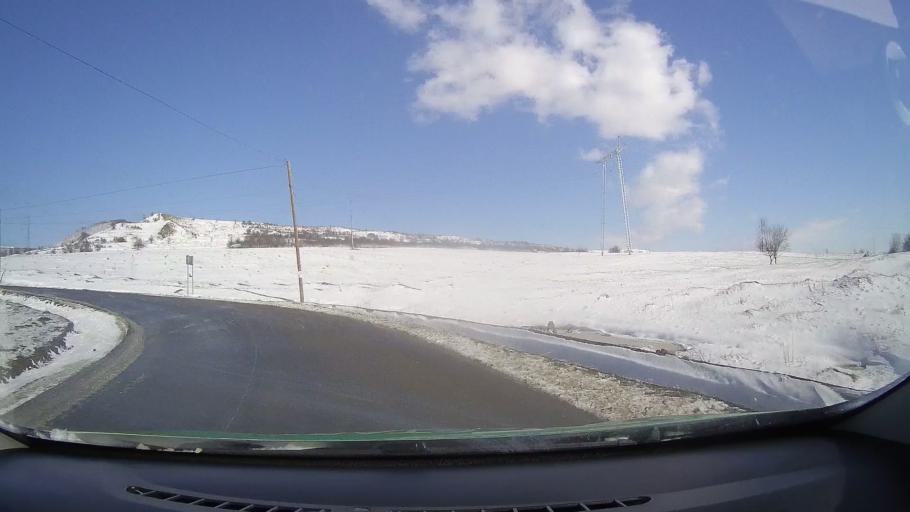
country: RO
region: Sibiu
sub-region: Comuna Avrig
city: Avrig
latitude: 45.7656
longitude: 24.3888
